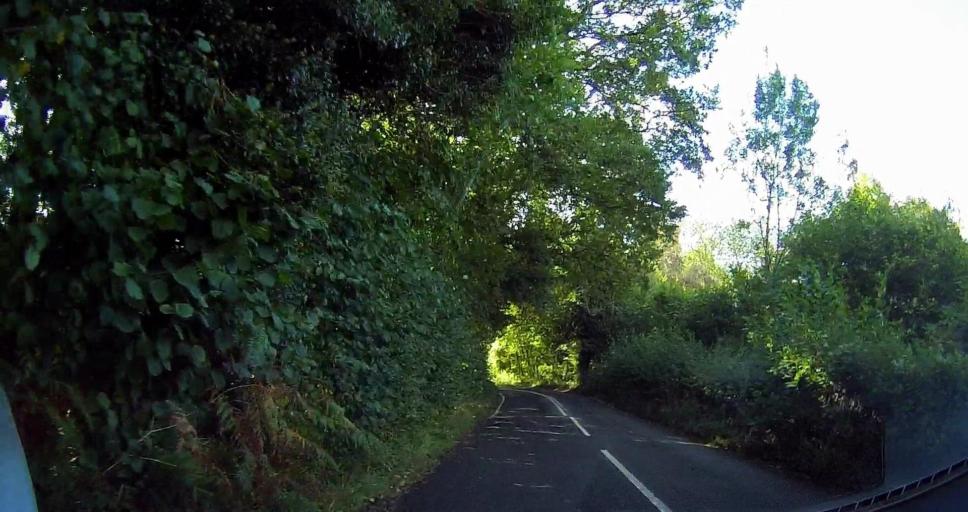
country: GB
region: England
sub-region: Kent
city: Borough Green
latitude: 51.3150
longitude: 0.2807
